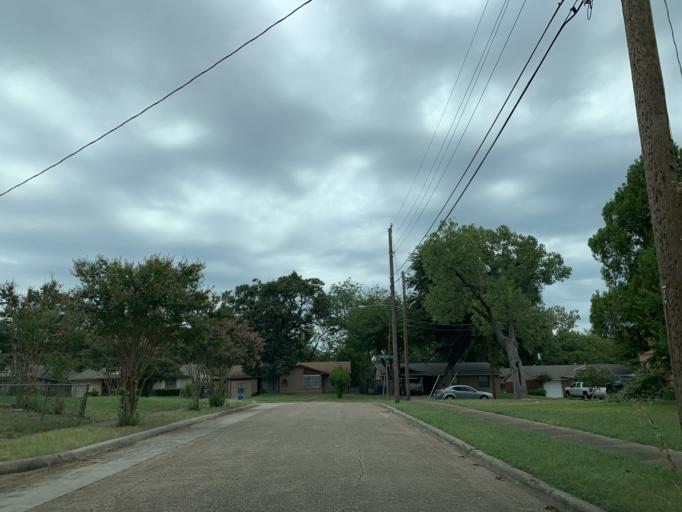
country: US
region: Texas
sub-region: Dallas County
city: DeSoto
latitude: 32.6578
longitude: -96.8252
